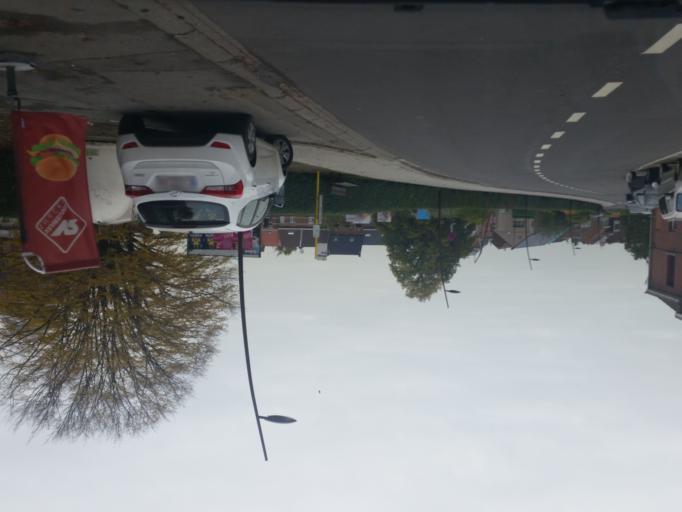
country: BE
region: Flanders
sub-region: Provincie Vlaams-Brabant
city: Beersel
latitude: 50.7642
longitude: 4.2762
